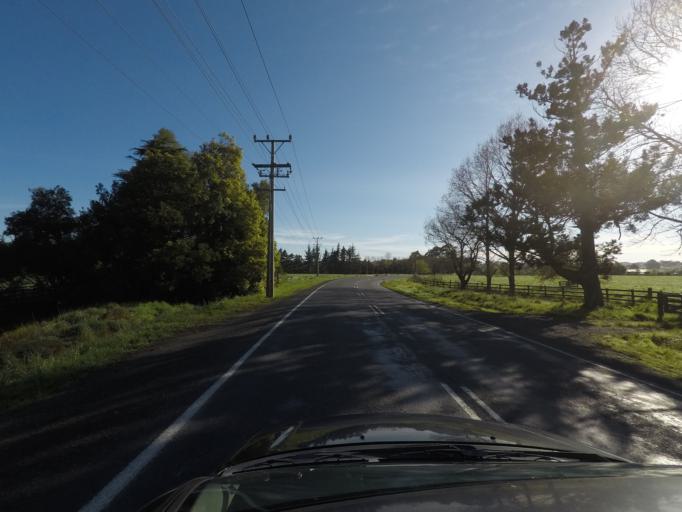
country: NZ
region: Auckland
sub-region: Auckland
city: Red Hill
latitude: -37.0035
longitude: 174.9567
